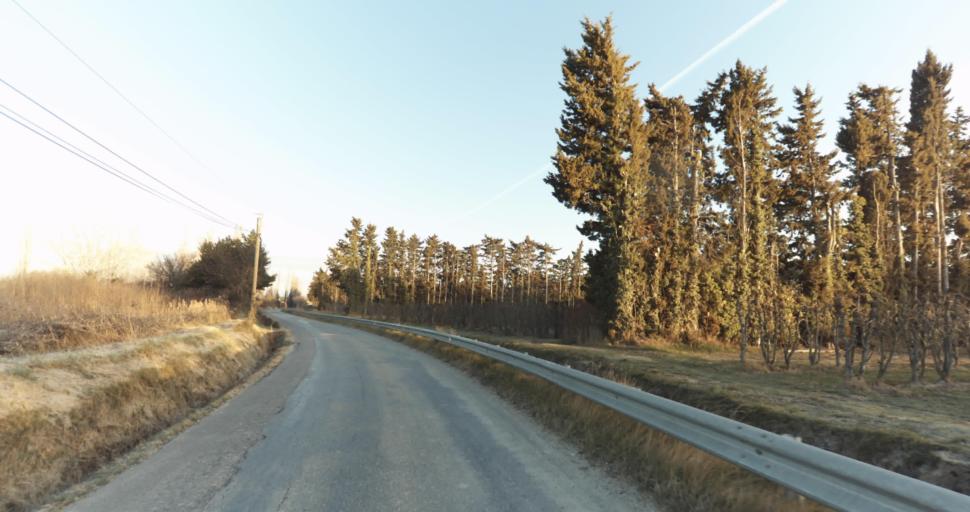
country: FR
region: Provence-Alpes-Cote d'Azur
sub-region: Departement des Bouches-du-Rhone
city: Barbentane
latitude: 43.8944
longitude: 4.7721
